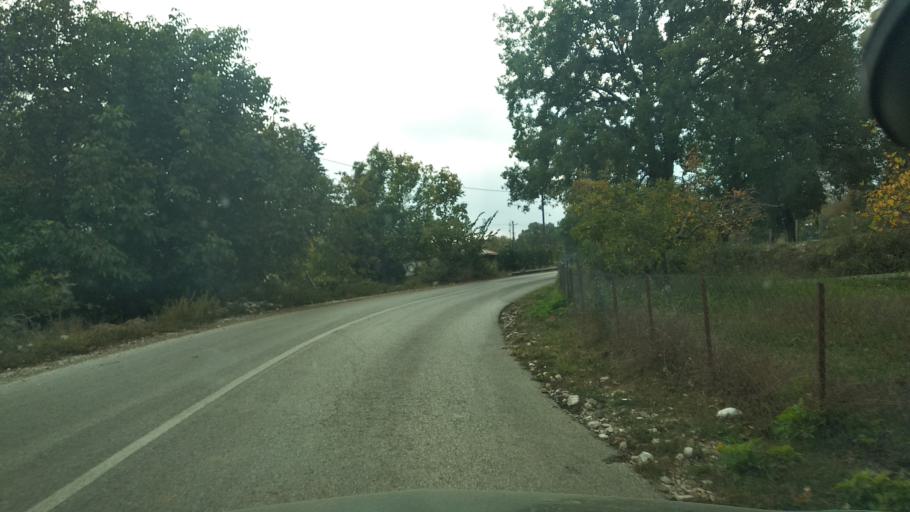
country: GR
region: Thessaly
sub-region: Trikala
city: Kastraki
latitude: 39.6945
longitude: 21.5217
